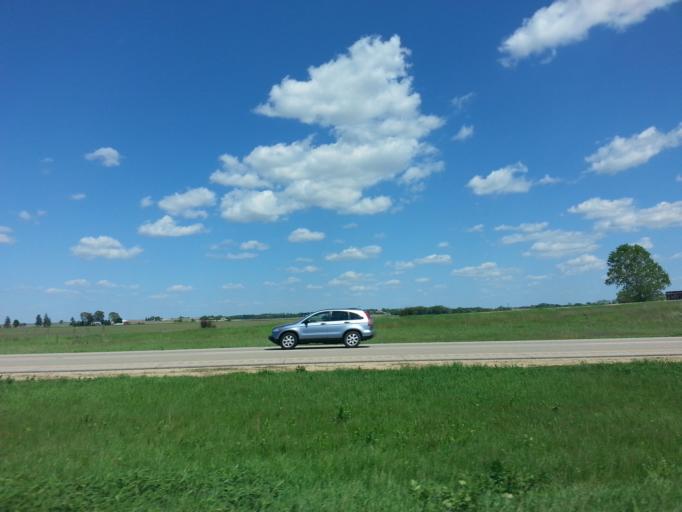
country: US
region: Wisconsin
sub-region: Rock County
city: Janesville
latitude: 42.6366
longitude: -88.9829
